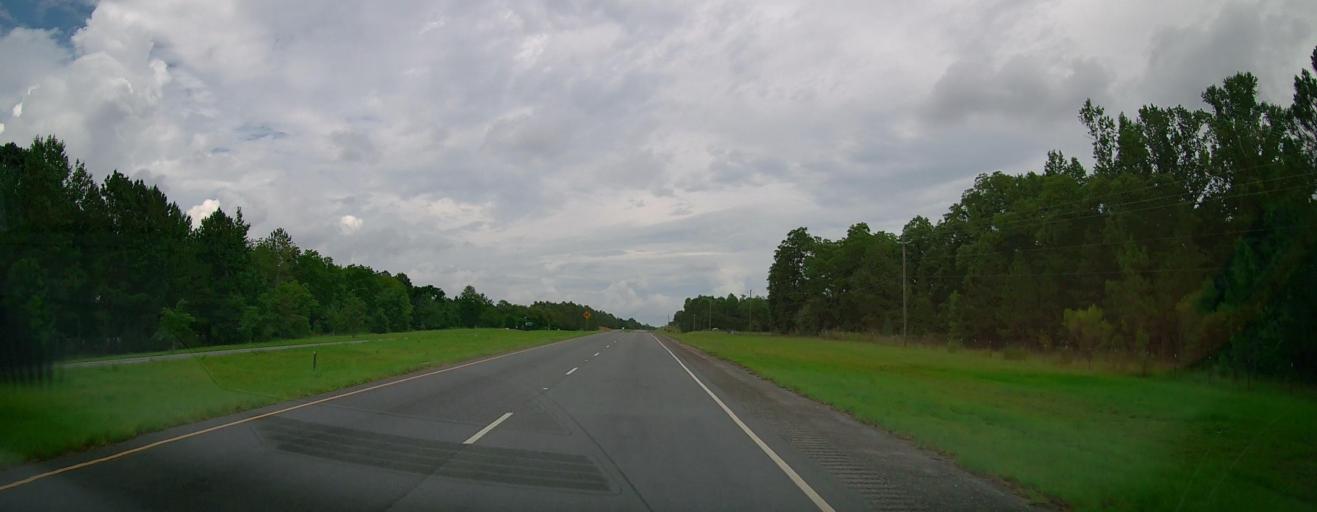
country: US
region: Georgia
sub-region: Telfair County
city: Helena
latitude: 32.1025
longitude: -83.0341
